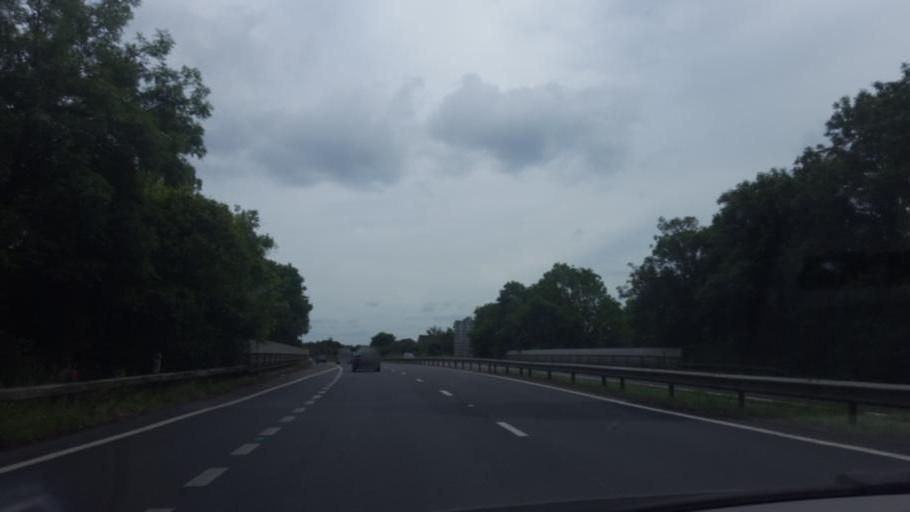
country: GB
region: England
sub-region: Royal Borough of Windsor and Maidenhead
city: White Waltham
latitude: 51.5162
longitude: -0.7625
